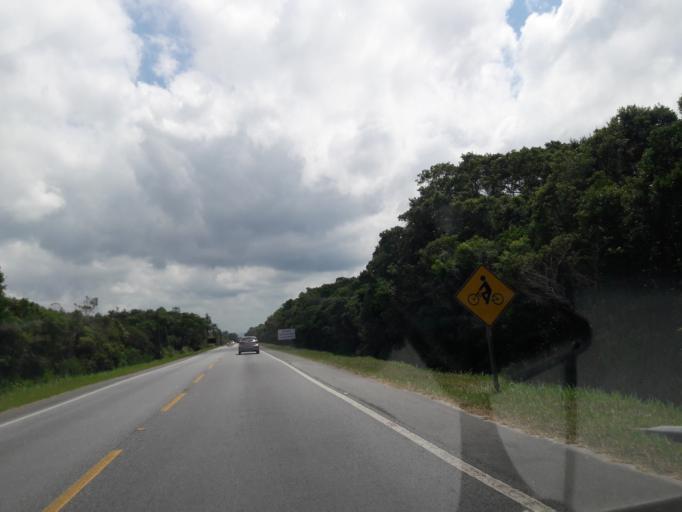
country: BR
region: Parana
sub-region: Pontal Do Parana
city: Pontal do Parana
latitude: -25.6792
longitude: -48.5024
